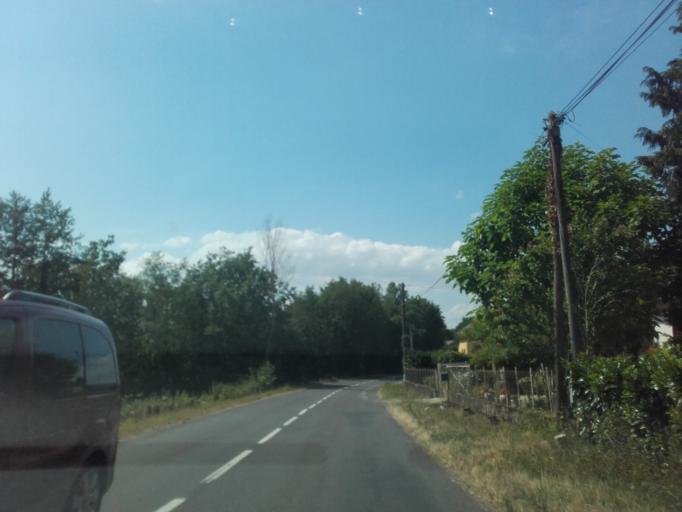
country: FR
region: Rhone-Alpes
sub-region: Departement de l'Ain
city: Chatillon-sur-Chalaronne
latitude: 46.1128
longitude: 4.9719
